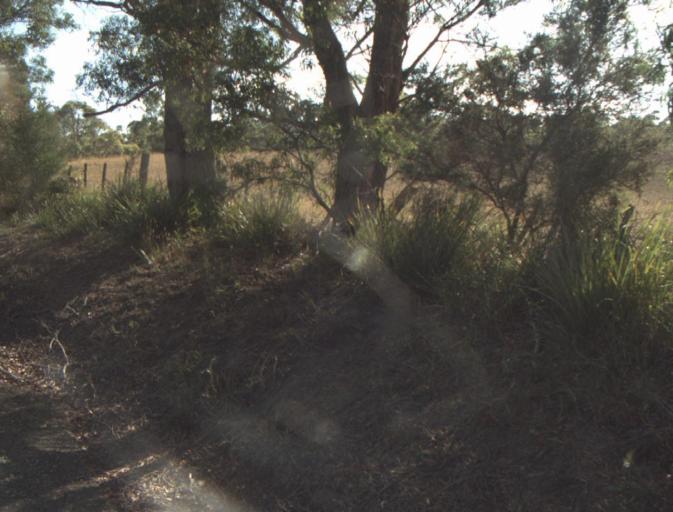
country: AU
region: Tasmania
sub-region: Dorset
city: Bridport
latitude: -41.1498
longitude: 147.2317
